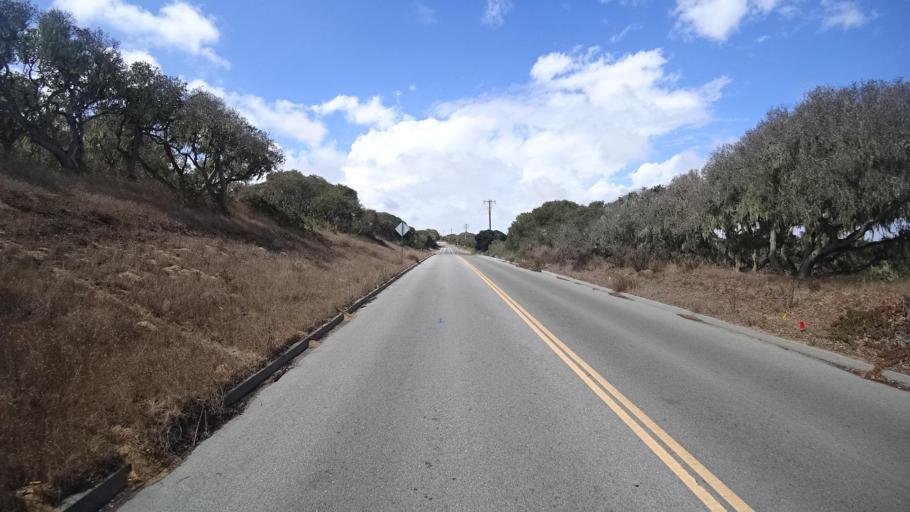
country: US
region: California
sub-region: Monterey County
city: Marina
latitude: 36.6552
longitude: -121.7441
